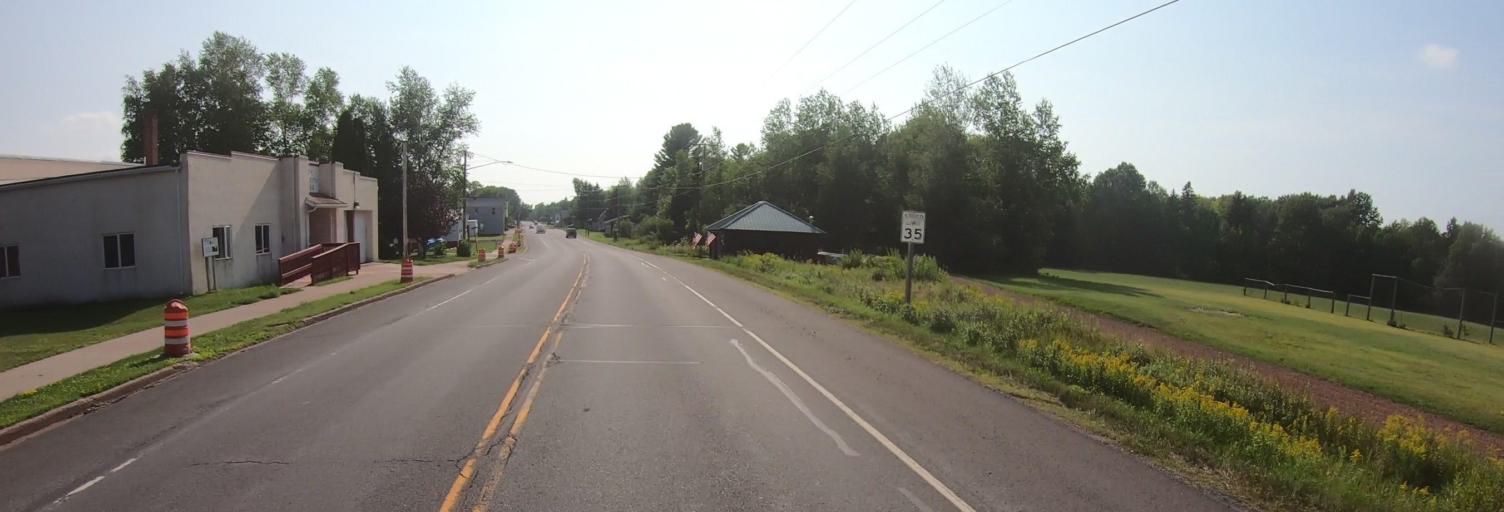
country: US
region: Wisconsin
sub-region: Iron County
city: Hurley
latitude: 46.4156
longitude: -90.2727
